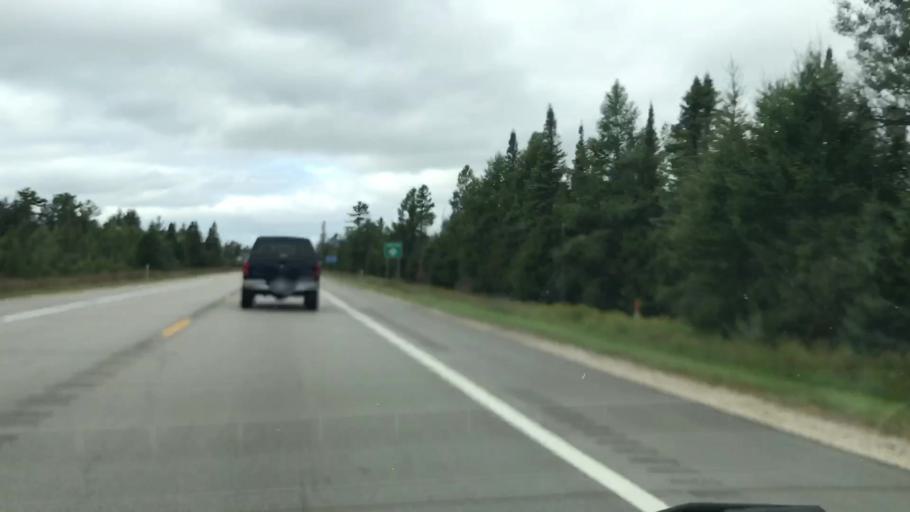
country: US
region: Michigan
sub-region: Schoolcraft County
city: Manistique
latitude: 45.8901
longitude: -86.5291
